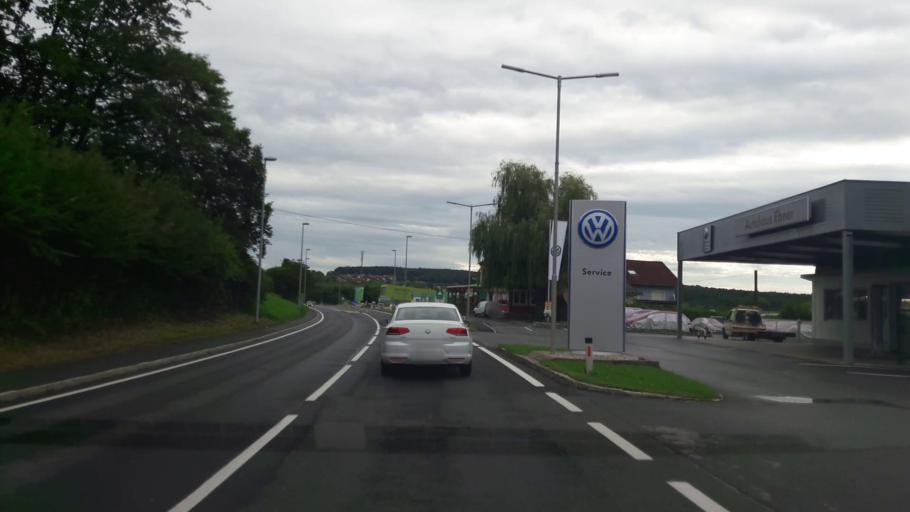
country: AT
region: Styria
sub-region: Politischer Bezirk Hartberg-Fuerstenfeld
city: Kaindorf
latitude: 47.2175
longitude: 15.8987
